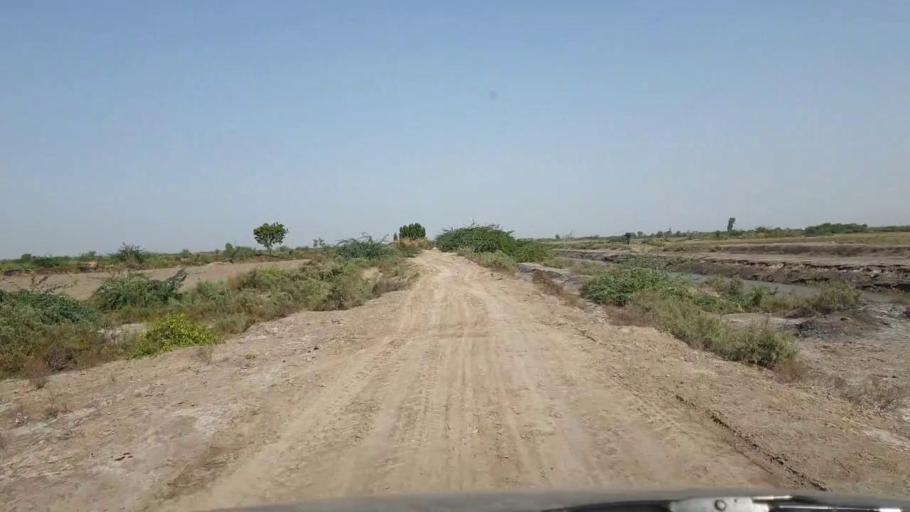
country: PK
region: Sindh
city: Tando Bago
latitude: 24.7018
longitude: 69.0707
